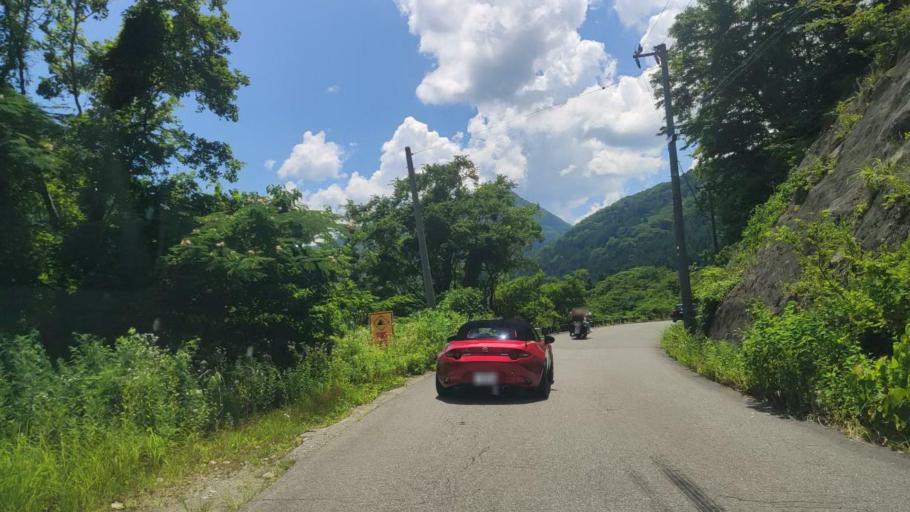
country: JP
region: Fukui
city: Ono
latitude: 35.8882
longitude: 136.5063
